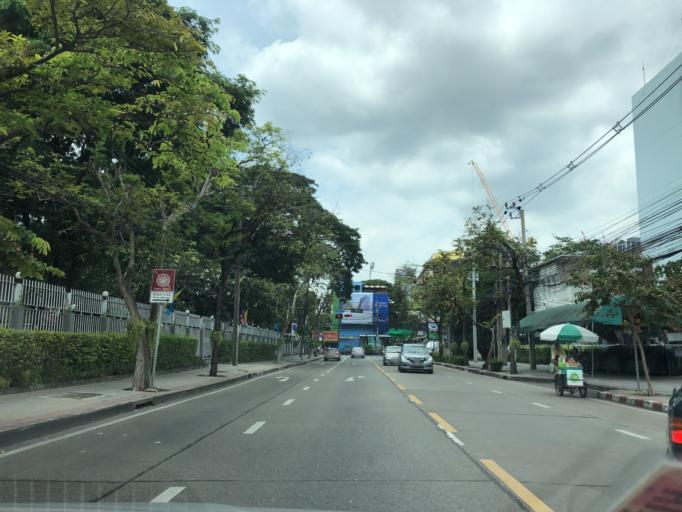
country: TH
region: Bangkok
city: Sathon
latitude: 13.7152
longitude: 100.5393
